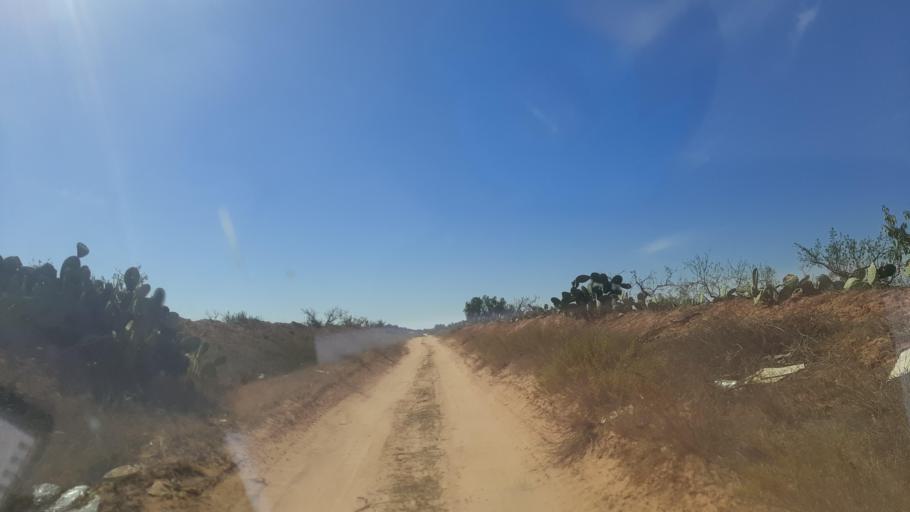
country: TN
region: Safaqis
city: Sfax
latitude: 34.8273
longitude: 10.5549
